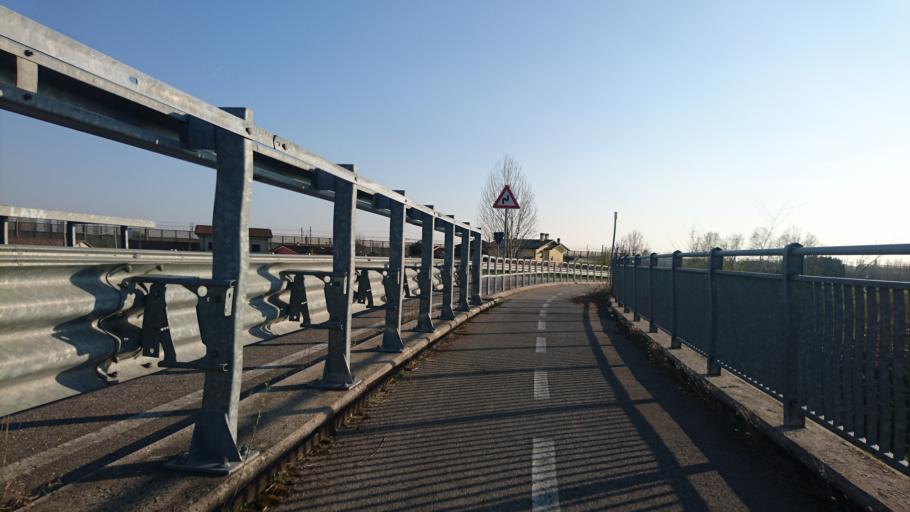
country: IT
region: Veneto
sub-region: Provincia di Padova
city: Vigonza
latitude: 45.4369
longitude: 11.9791
